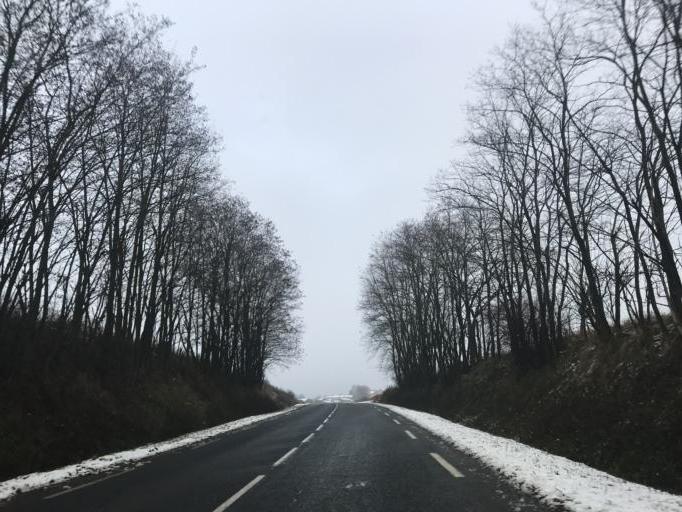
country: FR
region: Rhone-Alpes
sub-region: Departement de l'Ain
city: Miribel
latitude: 45.8372
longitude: 4.9445
